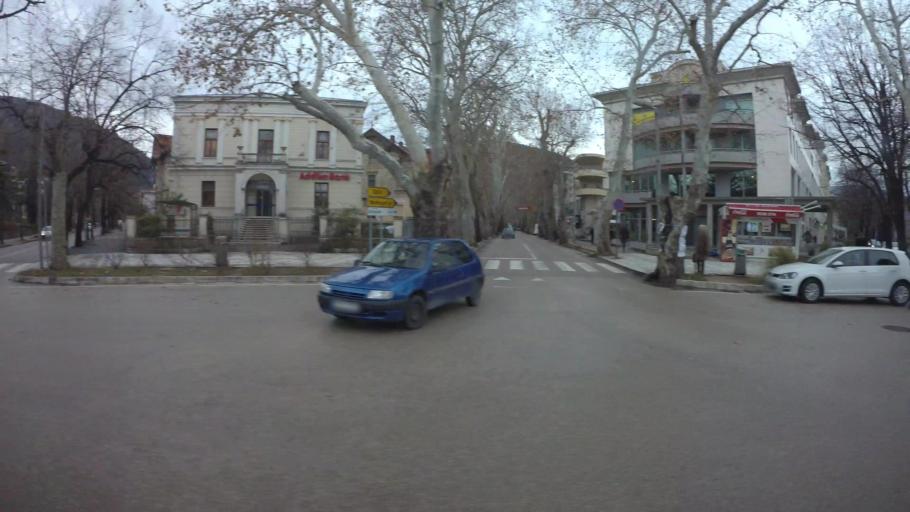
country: BA
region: Federation of Bosnia and Herzegovina
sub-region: Hercegovacko-Bosanski Kanton
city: Mostar
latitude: 43.3415
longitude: 17.8024
